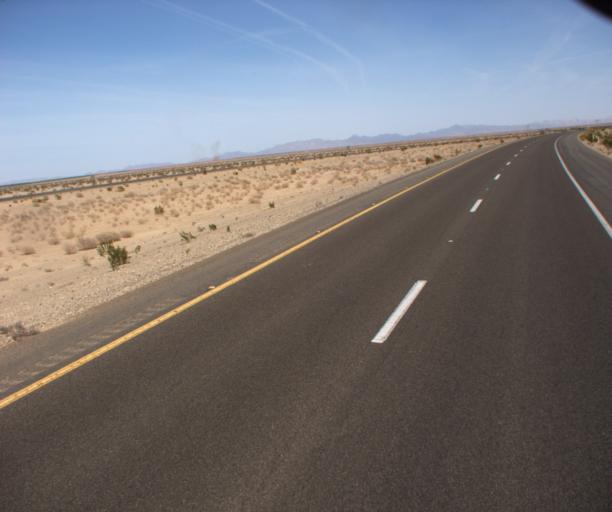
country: US
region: Arizona
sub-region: Yuma County
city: Somerton
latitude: 32.4959
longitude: -114.6471
